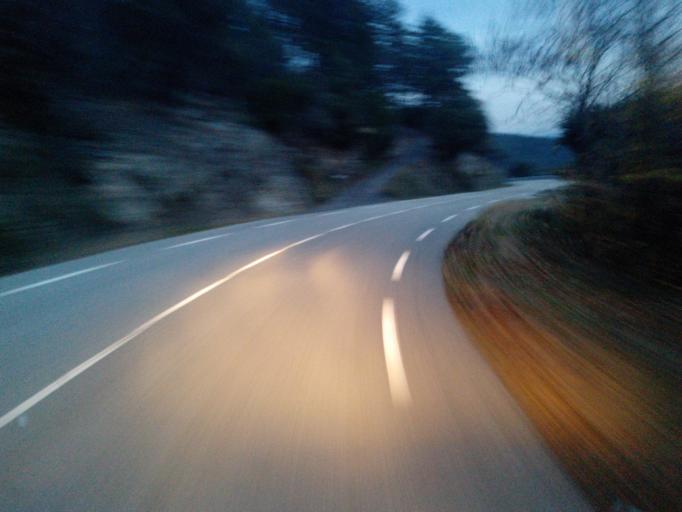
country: FR
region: Languedoc-Roussillon
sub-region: Departement du Gard
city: Saint-Jean-du-Gard
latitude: 44.1351
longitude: 3.8425
